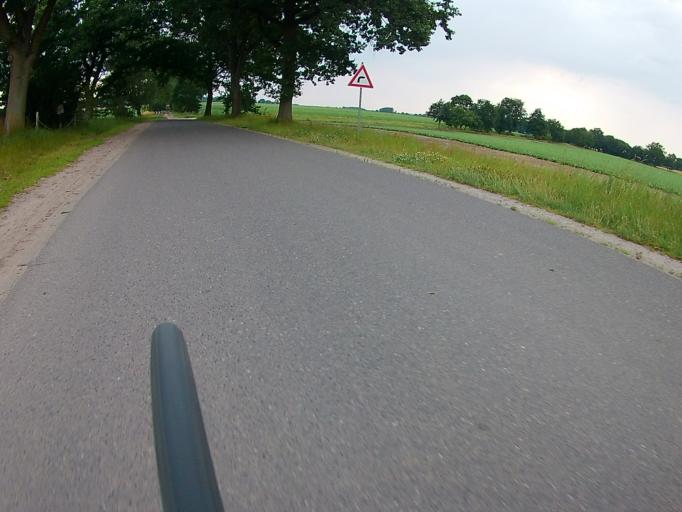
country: DE
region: Lower Saxony
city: Brackel
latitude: 53.2989
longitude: 10.0304
